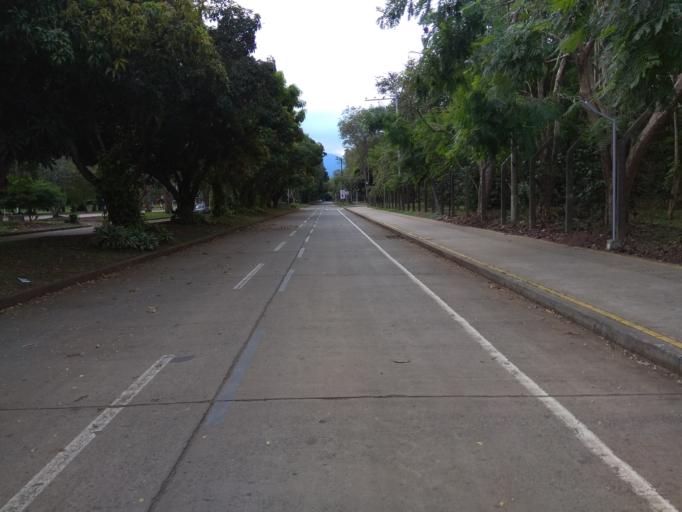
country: CO
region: Valle del Cauca
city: Cali
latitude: 3.3726
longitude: -76.5311
